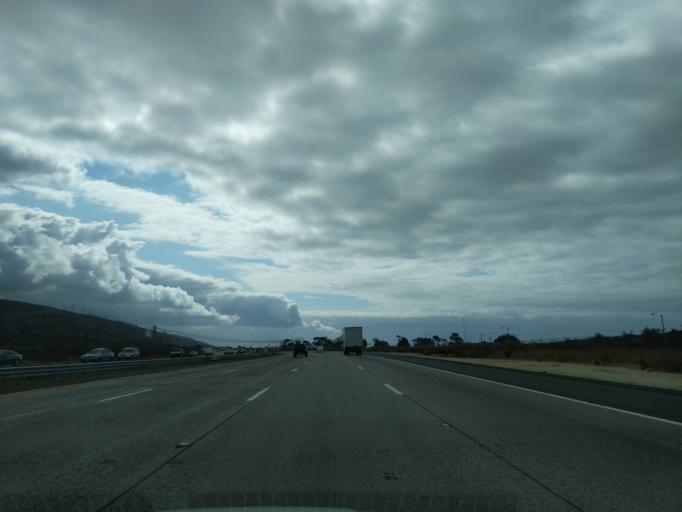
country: US
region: California
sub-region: Orange County
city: San Clemente
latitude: 33.3764
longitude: -117.5632
